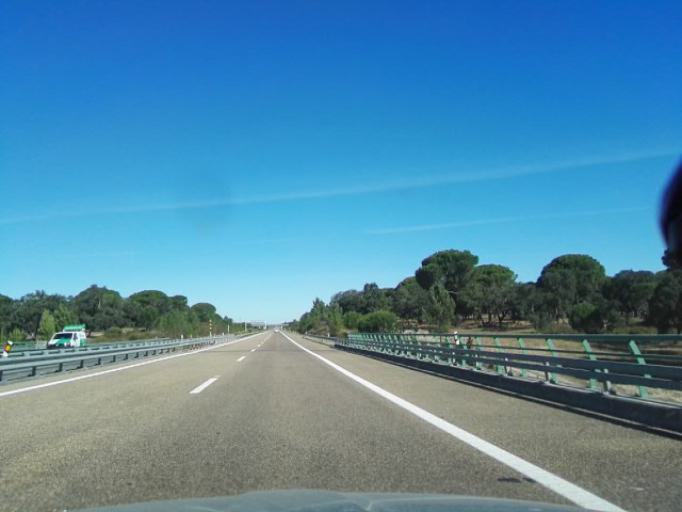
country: PT
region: Evora
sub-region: Vendas Novas
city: Vendas Novas
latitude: 38.6129
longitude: -8.6503
